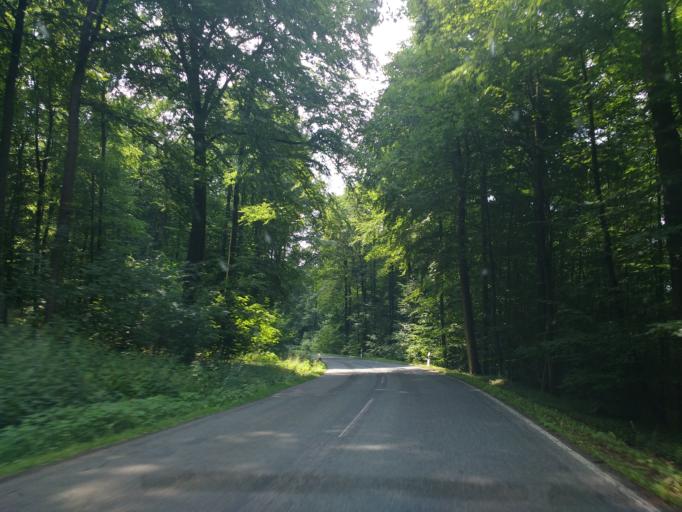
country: DE
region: North Rhine-Westphalia
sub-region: Regierungsbezirk Detmold
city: Dorentrup
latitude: 52.0468
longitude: 9.0401
